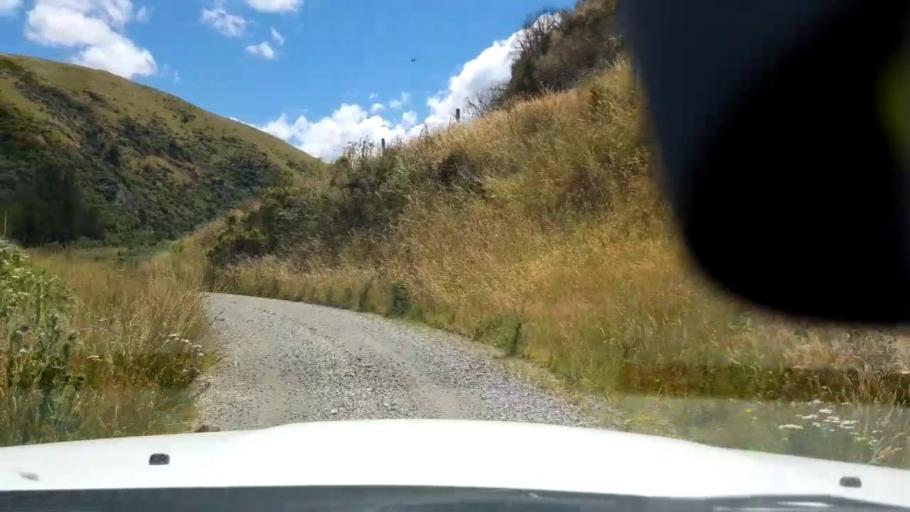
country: NZ
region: Canterbury
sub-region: Timaru District
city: Pleasant Point
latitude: -43.9331
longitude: 171.1973
